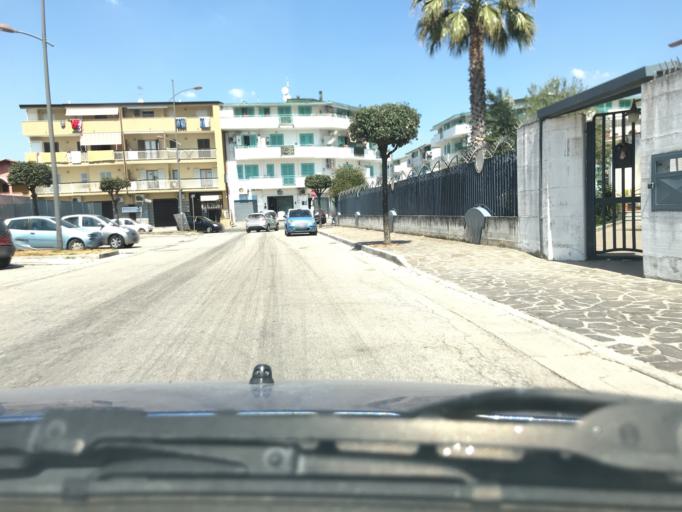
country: IT
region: Campania
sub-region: Provincia di Napoli
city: Villaricca
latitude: 40.9181
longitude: 14.1766
